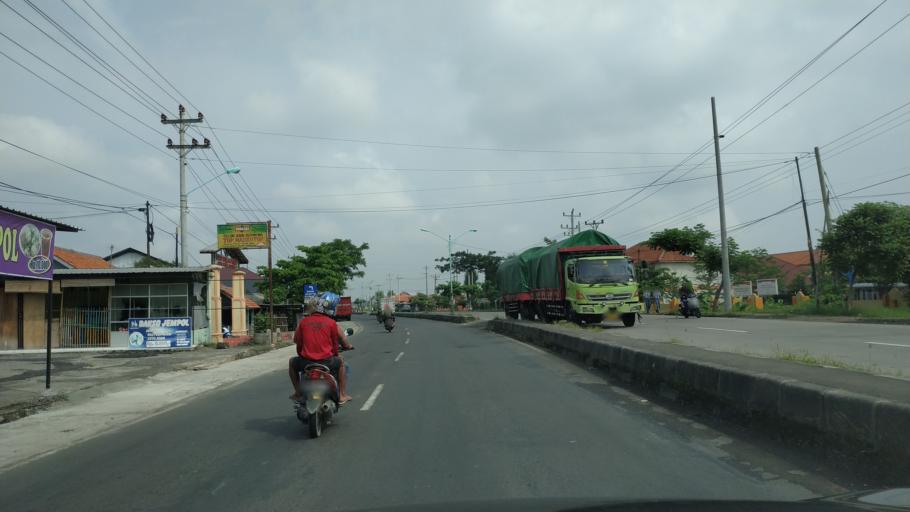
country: ID
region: Central Java
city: Bulakamba
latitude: -6.8728
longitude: 108.9114
